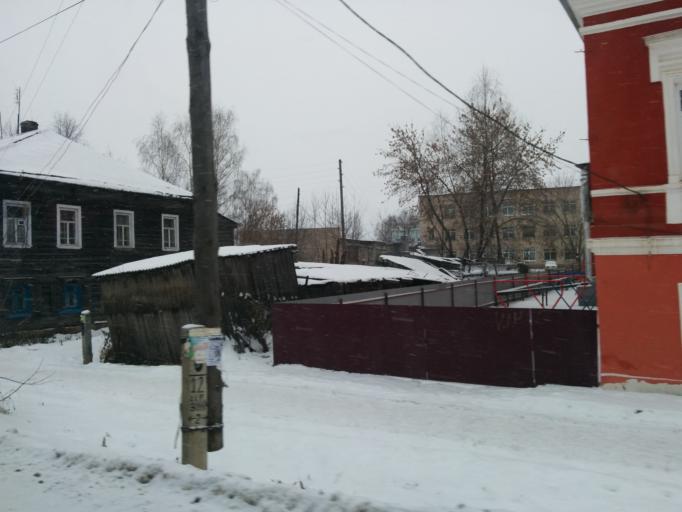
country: RU
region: Perm
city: Okhansk
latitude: 57.7232
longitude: 55.3898
